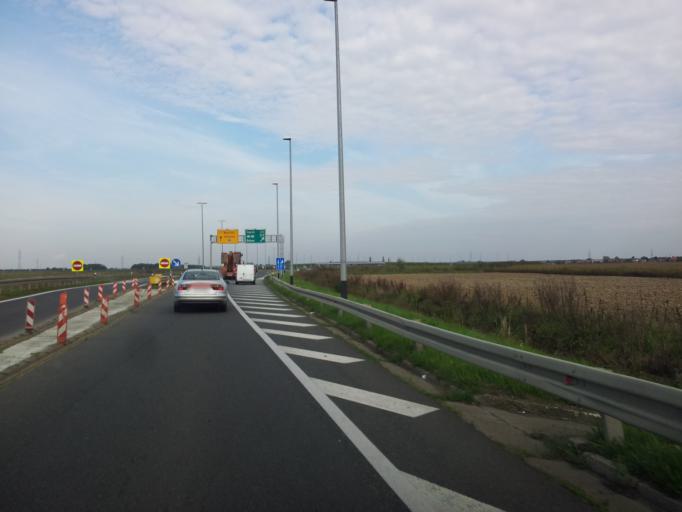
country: HR
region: Osjecko-Baranjska
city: Josipovac
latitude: 45.5727
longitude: 18.5753
